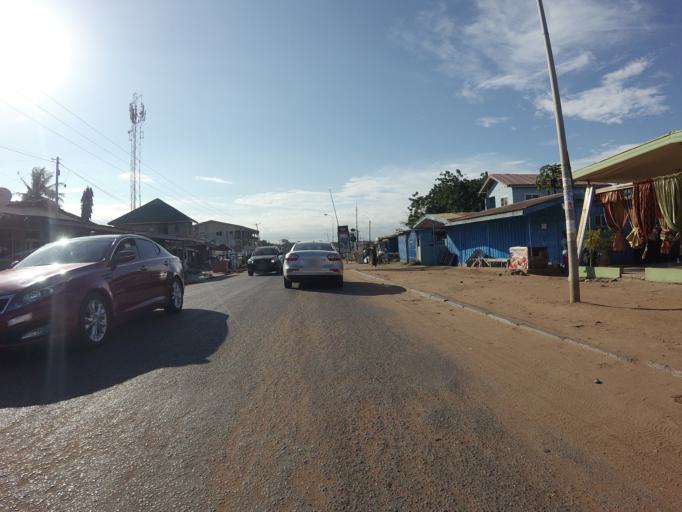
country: GH
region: Greater Accra
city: Nungua
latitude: 5.6483
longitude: -0.0625
